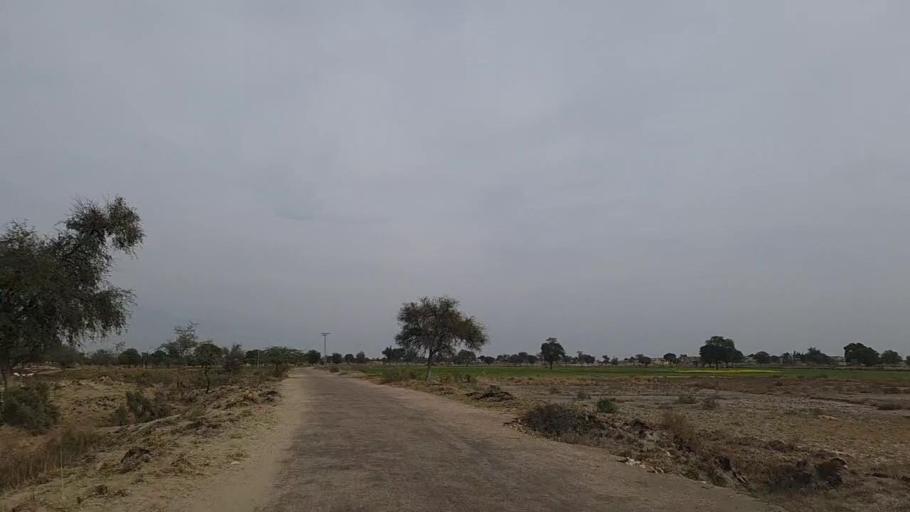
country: PK
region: Sindh
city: Jam Sahib
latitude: 26.3997
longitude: 68.5135
